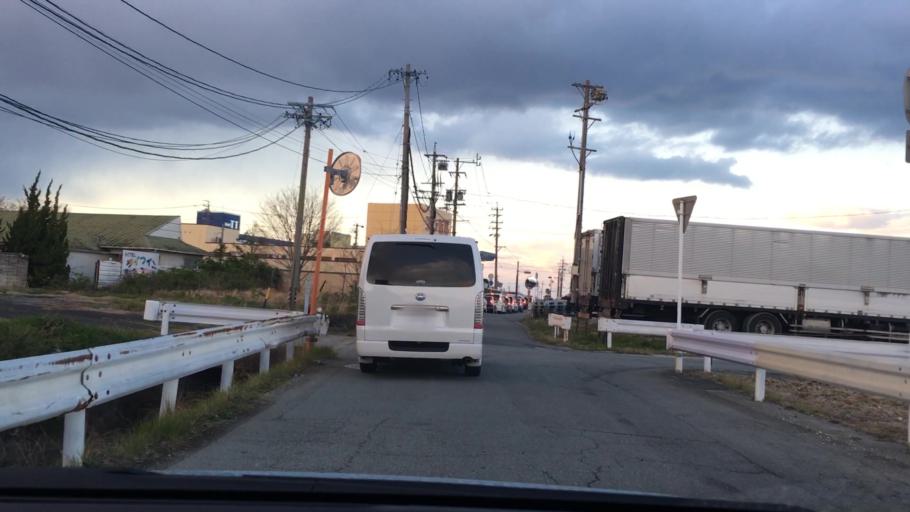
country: JP
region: Mie
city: Ise
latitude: 34.5331
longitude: 136.6783
